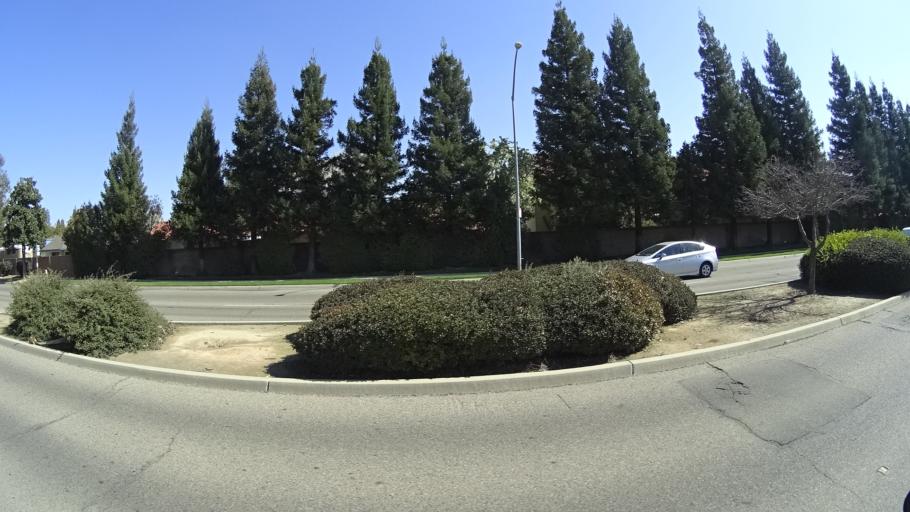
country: US
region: California
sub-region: Fresno County
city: Clovis
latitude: 36.8463
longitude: -119.7569
